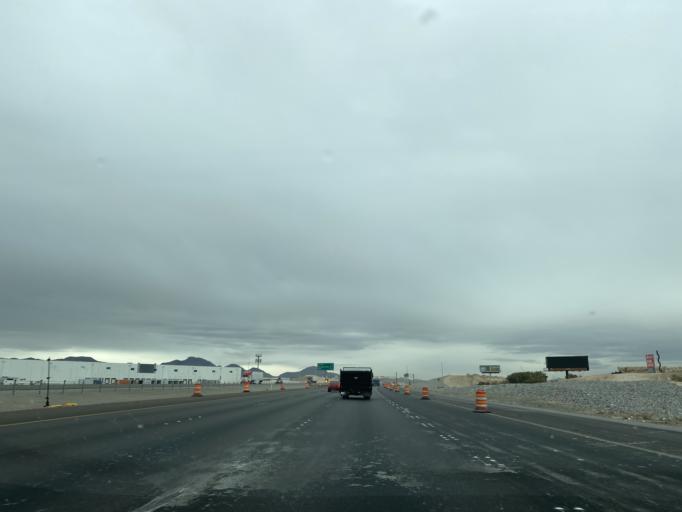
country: US
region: Nevada
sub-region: Clark County
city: Nellis Air Force Base
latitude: 36.2642
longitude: -115.0707
